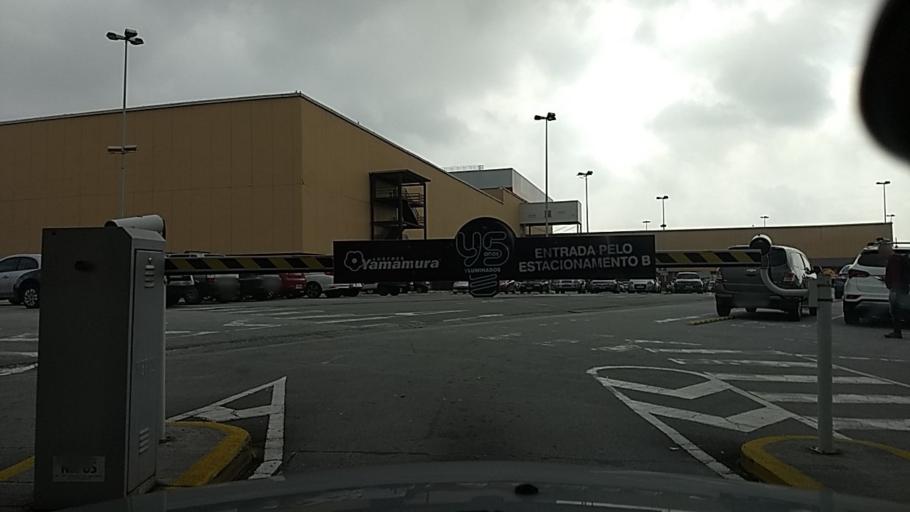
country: BR
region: Sao Paulo
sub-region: Sao Paulo
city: Sao Paulo
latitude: -23.5157
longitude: -46.6147
